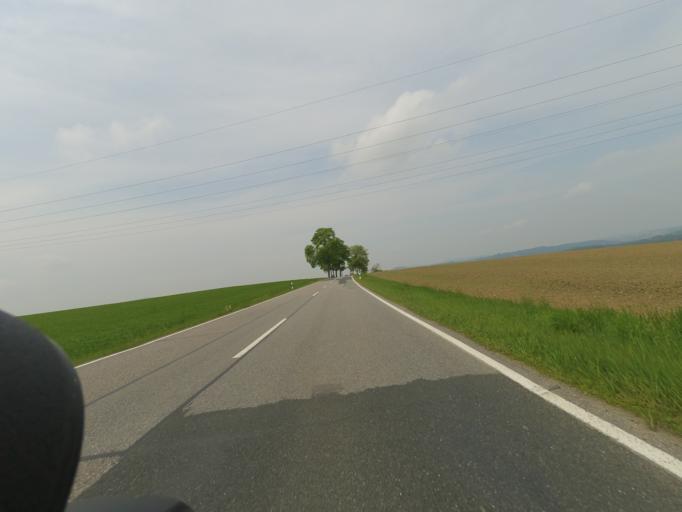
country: DE
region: Saxony
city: Wolkenstein
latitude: 50.6480
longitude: 13.0899
